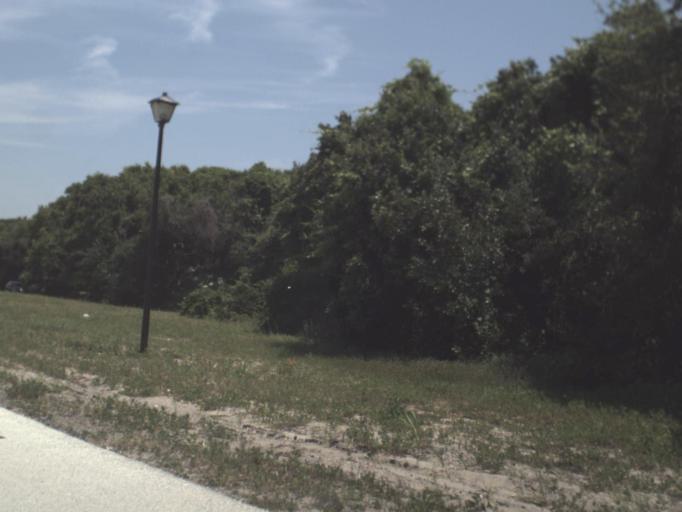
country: US
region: Florida
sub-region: Saint Johns County
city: Palm Valley
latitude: 30.1586
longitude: -81.3563
